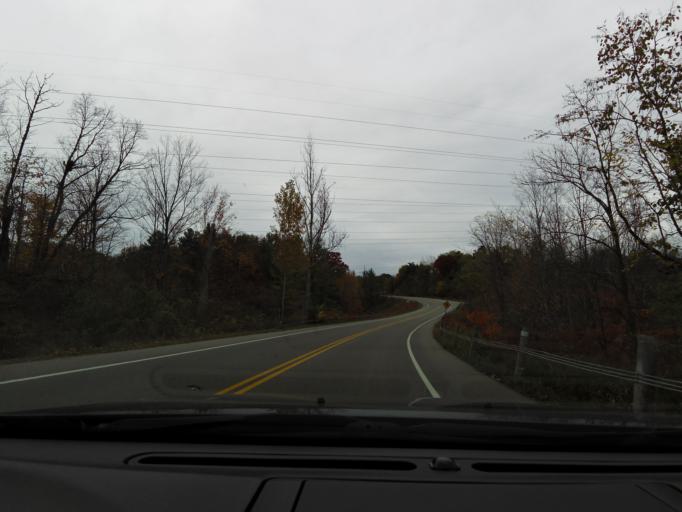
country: CA
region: Ontario
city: Hamilton
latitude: 43.3016
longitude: -79.8866
